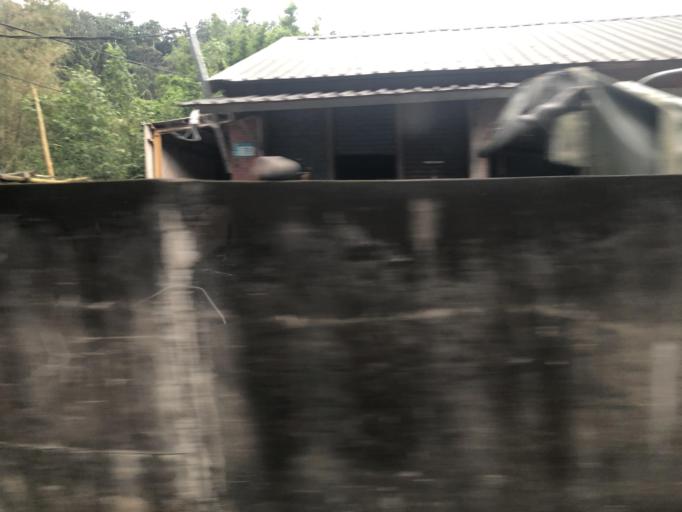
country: TW
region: Taiwan
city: Daxi
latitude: 24.9111
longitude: 121.3397
